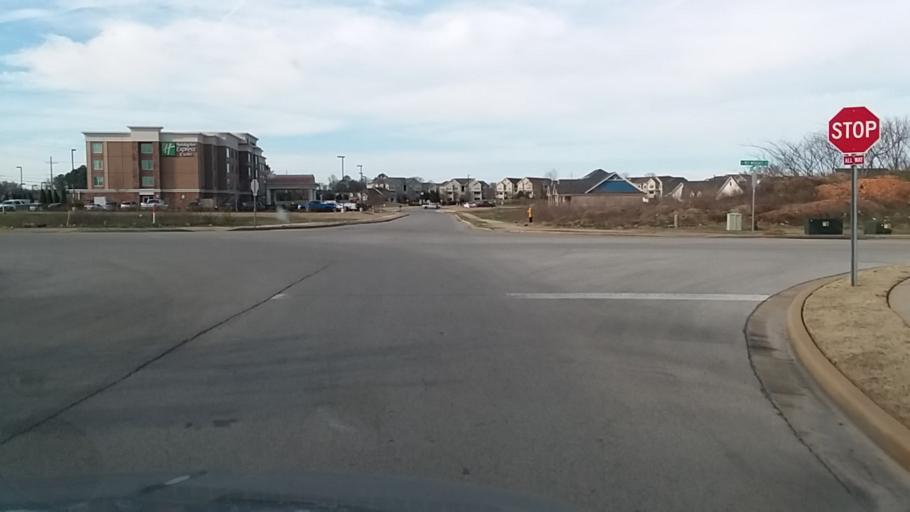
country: US
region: Alabama
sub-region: Madison County
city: Madison
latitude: 34.7575
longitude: -86.7132
